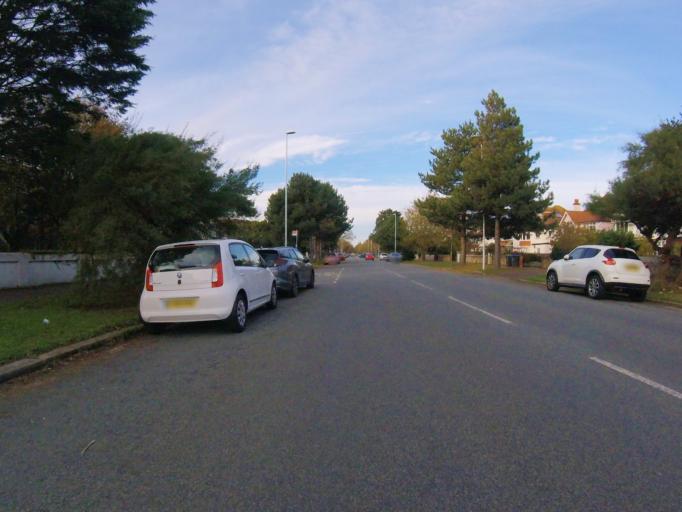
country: GB
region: England
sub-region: West Sussex
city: Worthing
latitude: 50.8082
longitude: -0.3924
